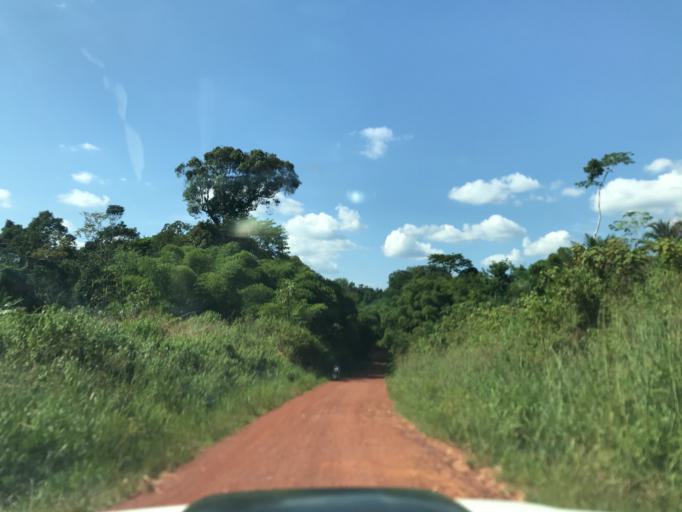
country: CD
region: Eastern Province
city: Kisangani
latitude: 1.2538
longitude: 25.2768
